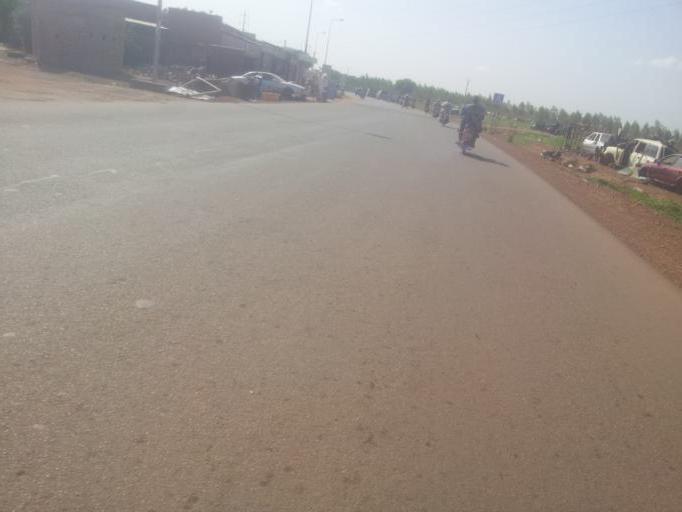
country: BF
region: Centre
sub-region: Kadiogo Province
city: Ouagadougou
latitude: 12.3702
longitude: -1.5662
